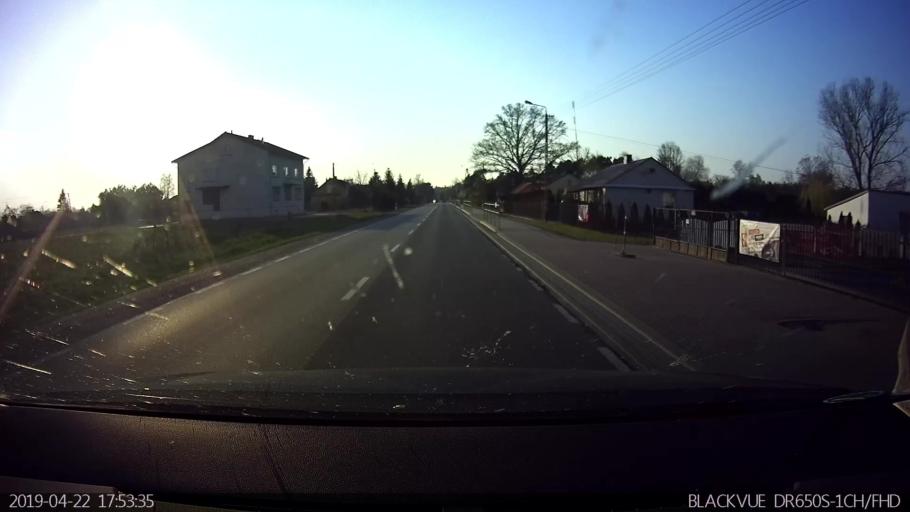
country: PL
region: Masovian Voivodeship
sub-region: Powiat wegrowski
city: Liw
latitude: 52.4541
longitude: 21.9521
